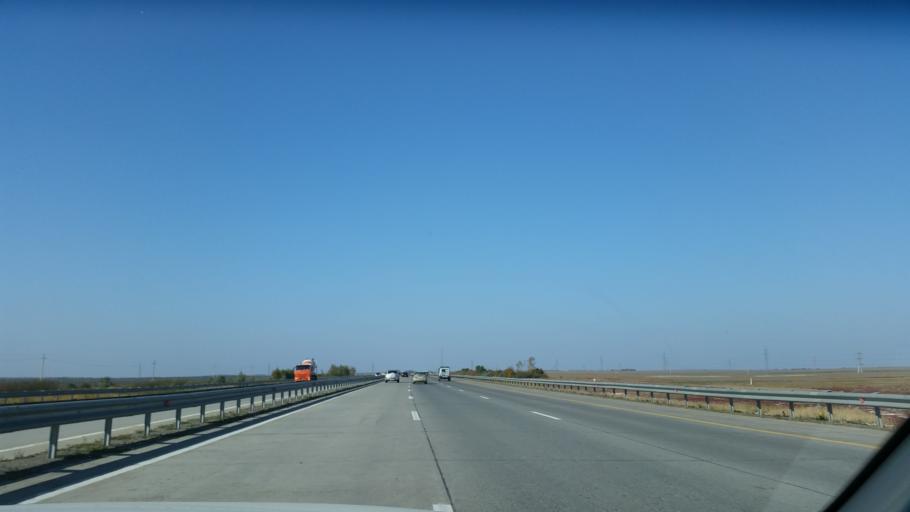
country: KZ
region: Astana Qalasy
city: Astana
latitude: 51.2765
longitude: 71.3651
